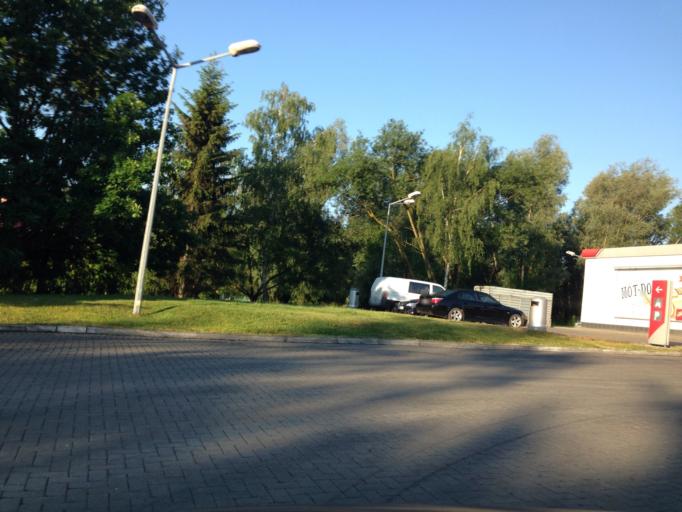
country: PL
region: Pomeranian Voivodeship
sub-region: Powiat kwidzynski
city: Kwidzyn
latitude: 53.7164
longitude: 18.9435
